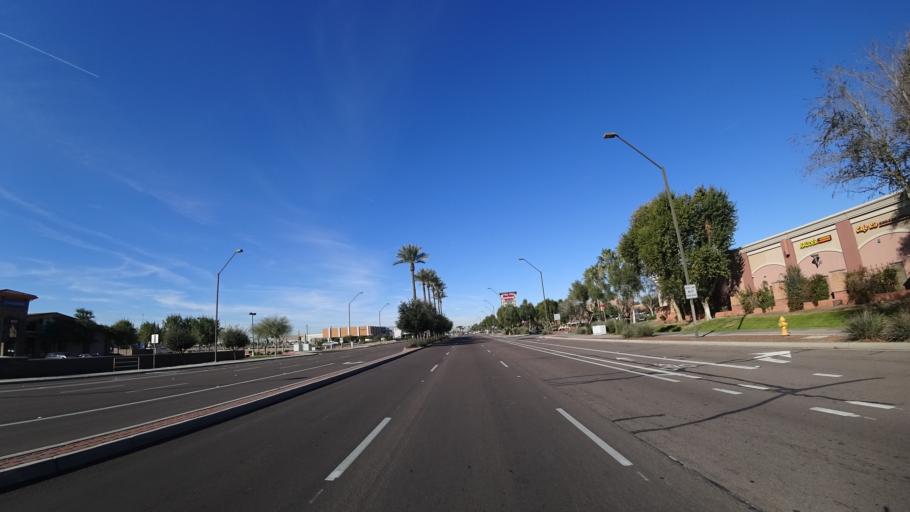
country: US
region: Arizona
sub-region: Maricopa County
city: Tolleson
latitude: 33.4647
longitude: -112.2773
